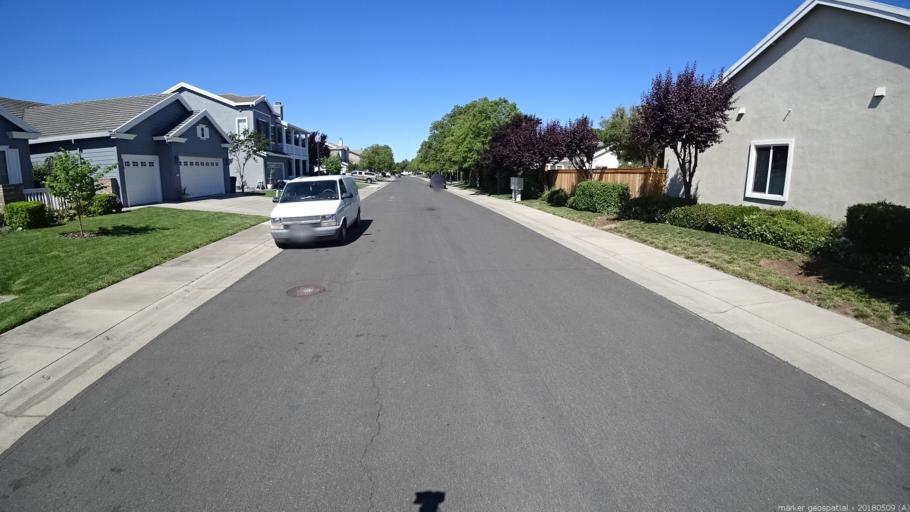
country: US
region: California
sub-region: Sacramento County
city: Elverta
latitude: 38.6735
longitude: -121.5200
